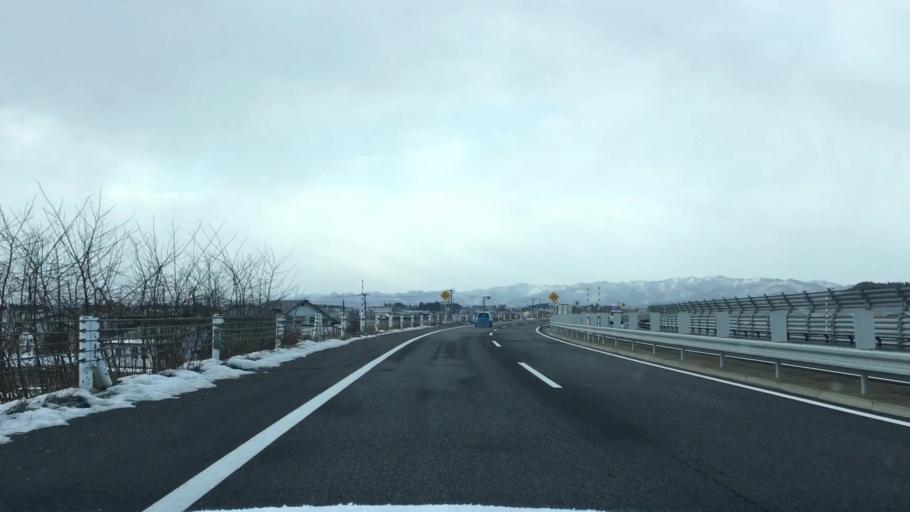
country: JP
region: Akita
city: Odate
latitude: 40.2938
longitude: 140.5526
